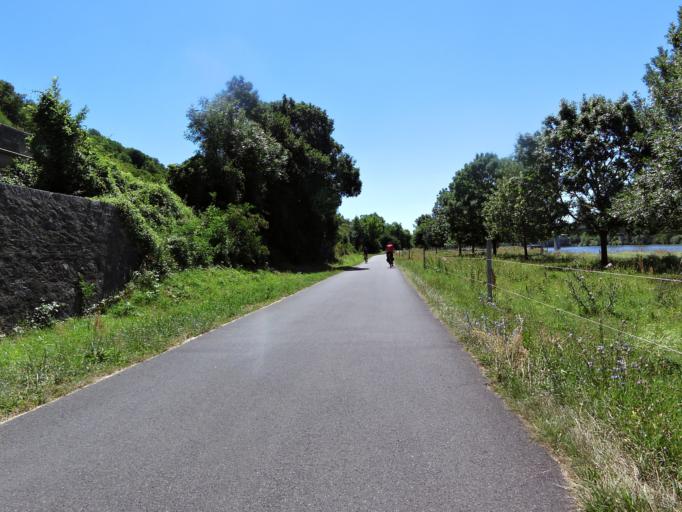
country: DE
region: Bavaria
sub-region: Regierungsbezirk Unterfranken
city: Sommerhausen
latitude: 49.6819
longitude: 10.0346
